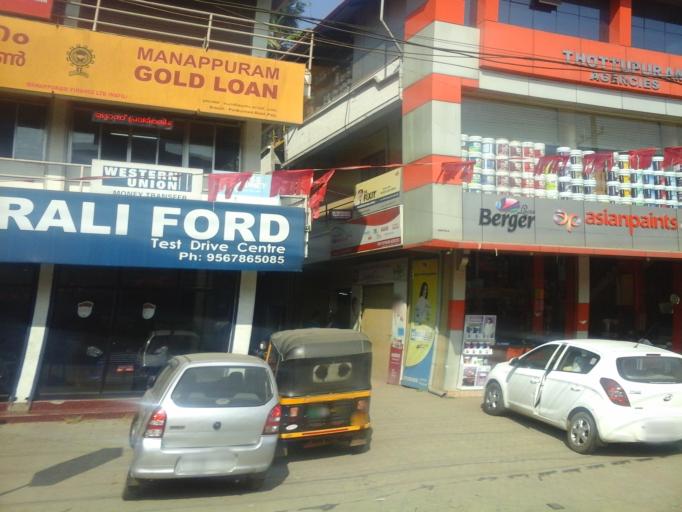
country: IN
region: Kerala
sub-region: Kottayam
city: Lalam
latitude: 9.7090
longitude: 76.6825
